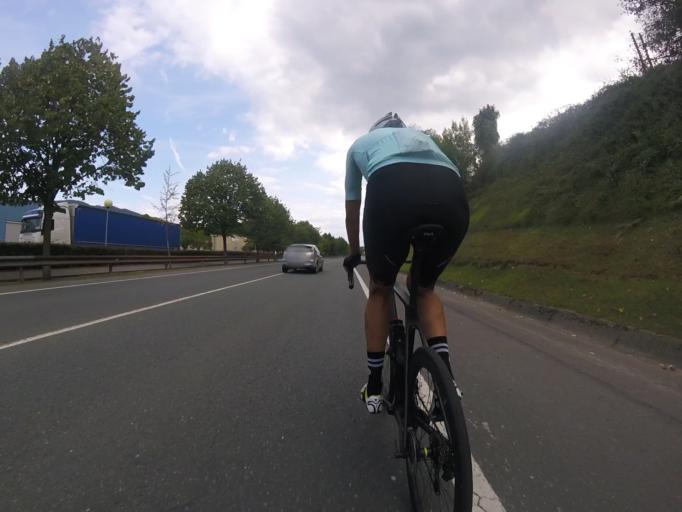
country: ES
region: Basque Country
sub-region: Provincia de Guipuzcoa
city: Aduna
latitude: 43.1956
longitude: -2.0531
